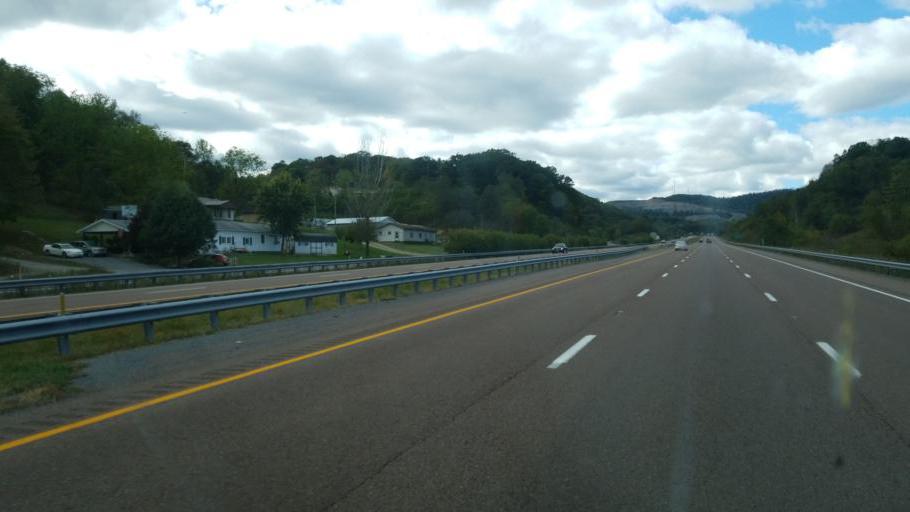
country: US
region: Maryland
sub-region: Allegany County
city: Cumberland
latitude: 39.7067
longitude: -78.5800
